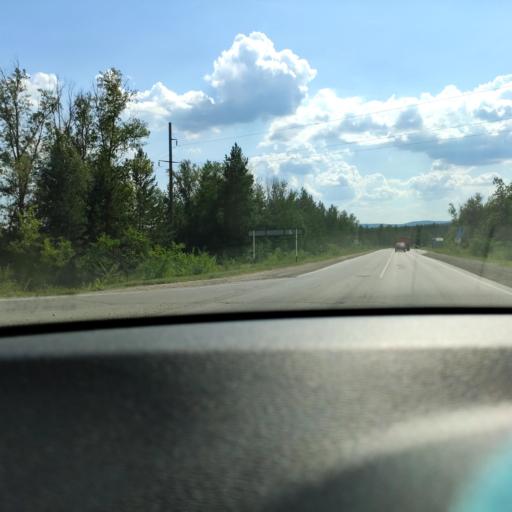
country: RU
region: Samara
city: Volzhskiy
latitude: 53.4574
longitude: 50.1669
